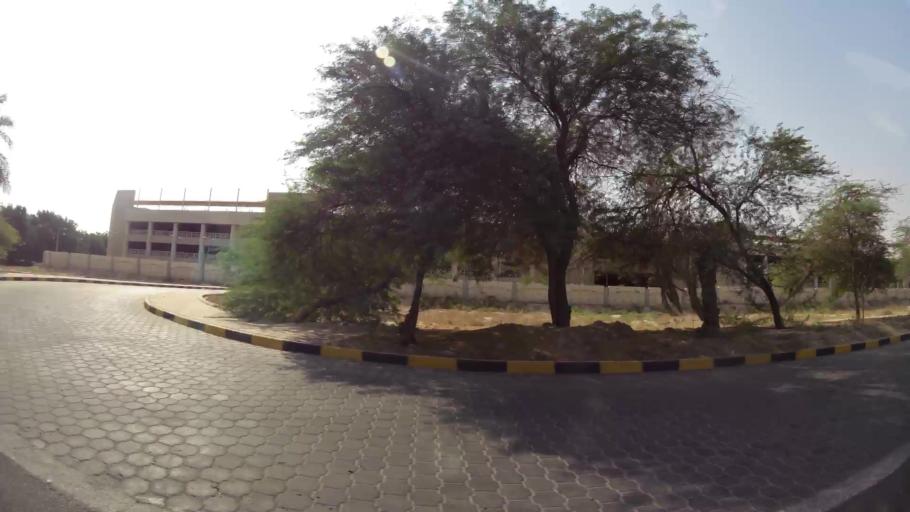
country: KW
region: Al Asimah
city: Ar Rabiyah
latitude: 29.2784
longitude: 47.9058
